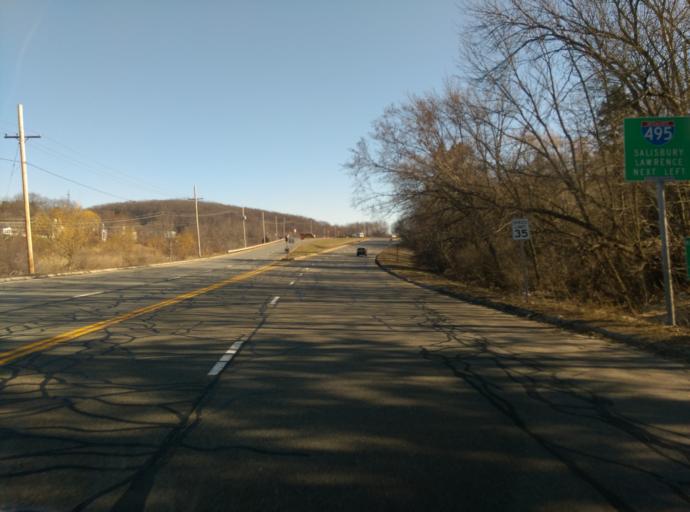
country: US
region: Massachusetts
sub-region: Essex County
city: Haverhill
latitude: 42.7475
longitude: -71.1093
